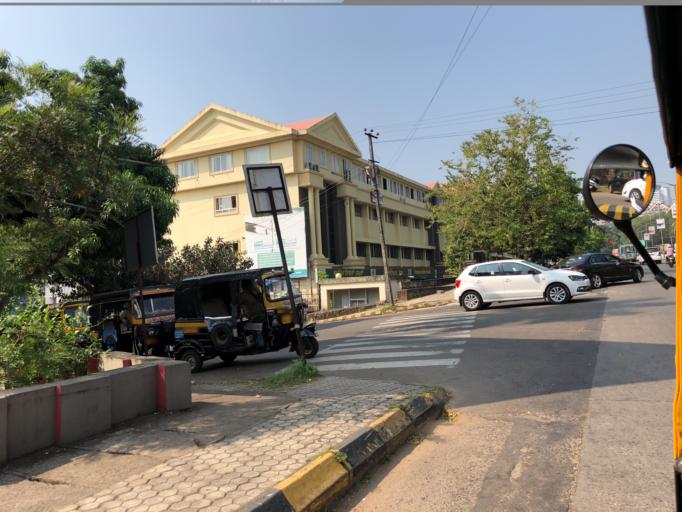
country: IN
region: Karnataka
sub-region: Dakshina Kannada
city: Mangalore
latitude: 12.8838
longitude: 74.8391
